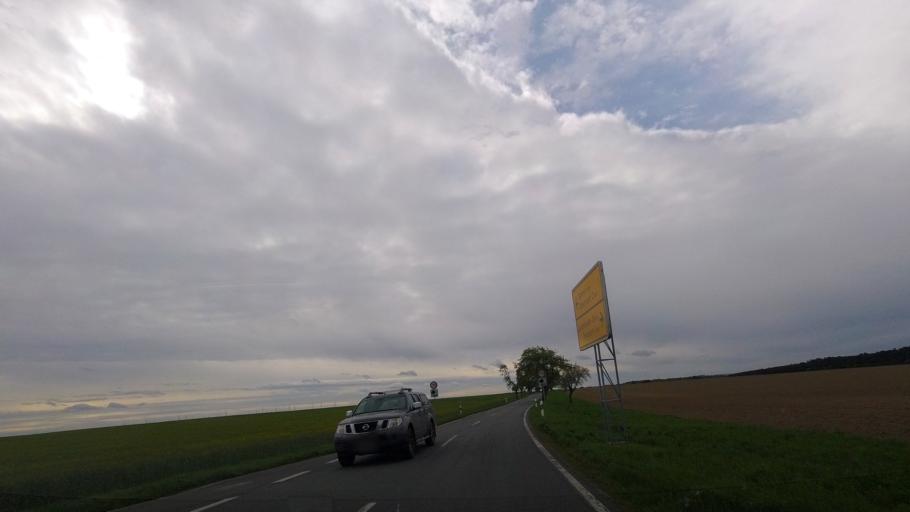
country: DE
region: Brandenburg
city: Dahme
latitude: 51.9141
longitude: 13.3998
